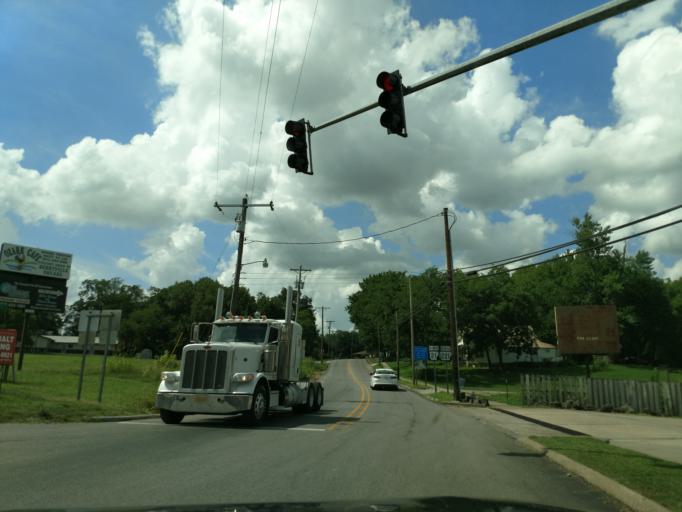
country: US
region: Arkansas
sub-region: Carroll County
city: Berryville
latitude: 36.3608
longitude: -93.5641
